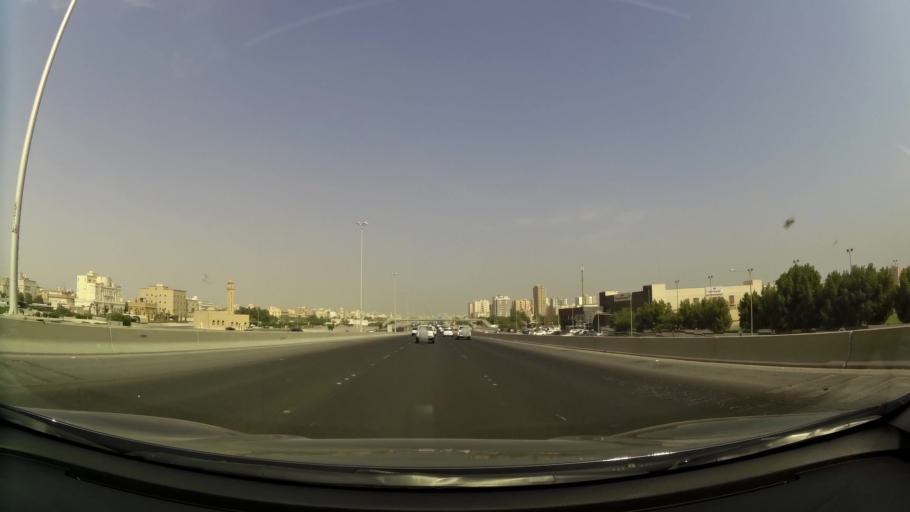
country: KW
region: Al Ahmadi
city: Al Manqaf
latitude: 29.0935
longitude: 48.1163
